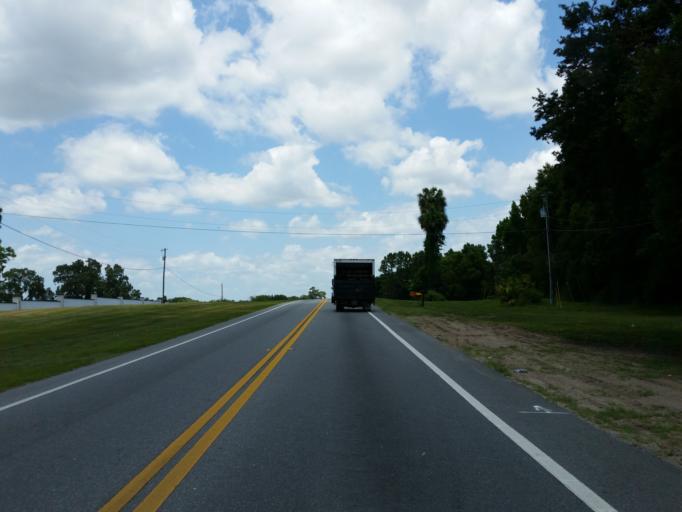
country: US
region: Florida
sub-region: Marion County
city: Belleview
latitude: 28.9930
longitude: -82.0413
